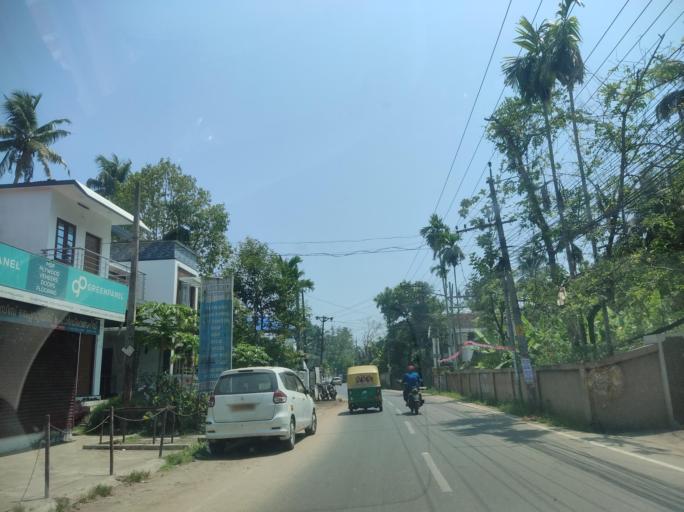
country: IN
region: Kerala
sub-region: Ernakulam
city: Cochin
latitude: 9.8907
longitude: 76.2852
